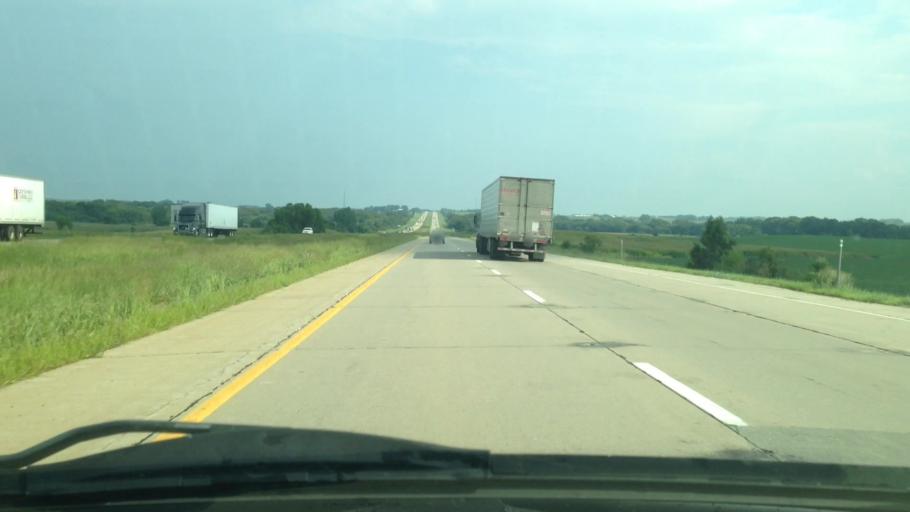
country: US
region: Iowa
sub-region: Benton County
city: Urbana
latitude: 42.3089
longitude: -91.9739
